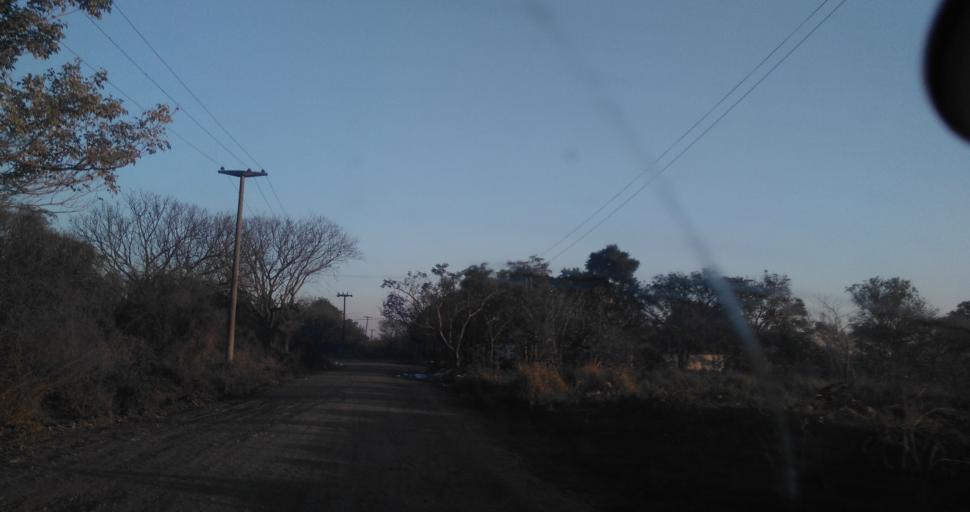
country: AR
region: Chaco
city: Fontana
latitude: -27.4255
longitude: -59.0120
